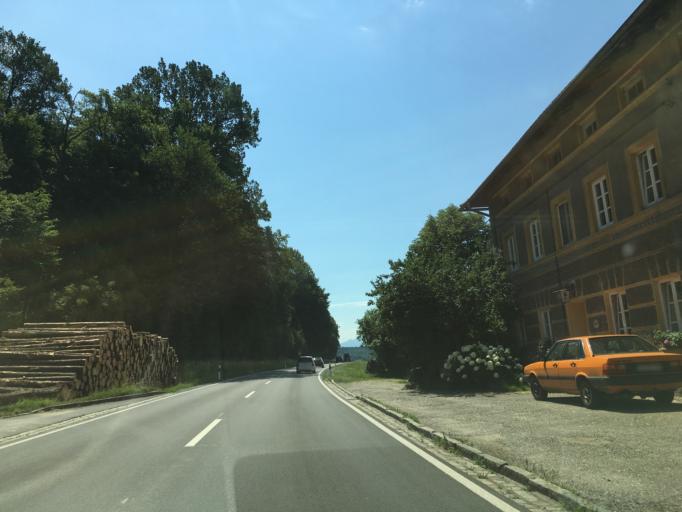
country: DE
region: Bavaria
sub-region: Upper Bavaria
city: Bad Endorf
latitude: 47.9304
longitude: 12.2865
